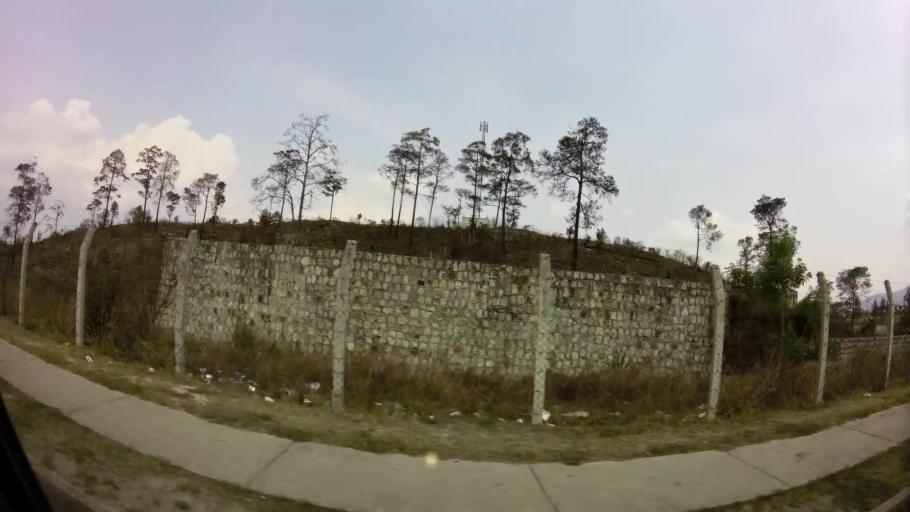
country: HN
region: Francisco Morazan
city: Tegucigalpa
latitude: 14.0614
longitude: -87.2547
